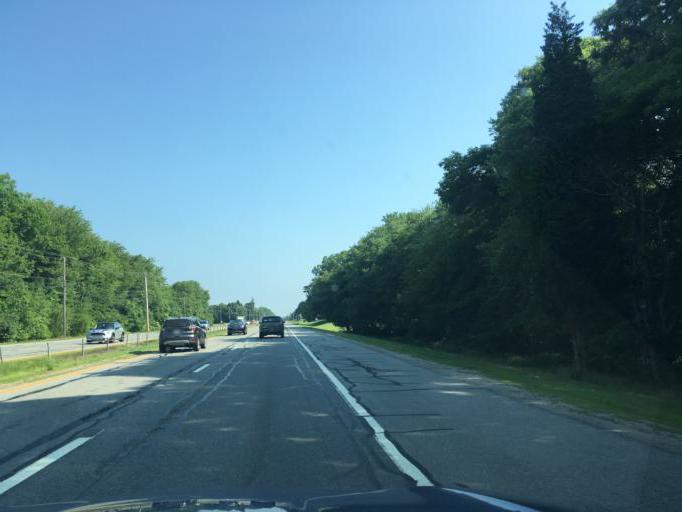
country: US
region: Rhode Island
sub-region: Washington County
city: North Kingstown
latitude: 41.5088
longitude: -71.4598
